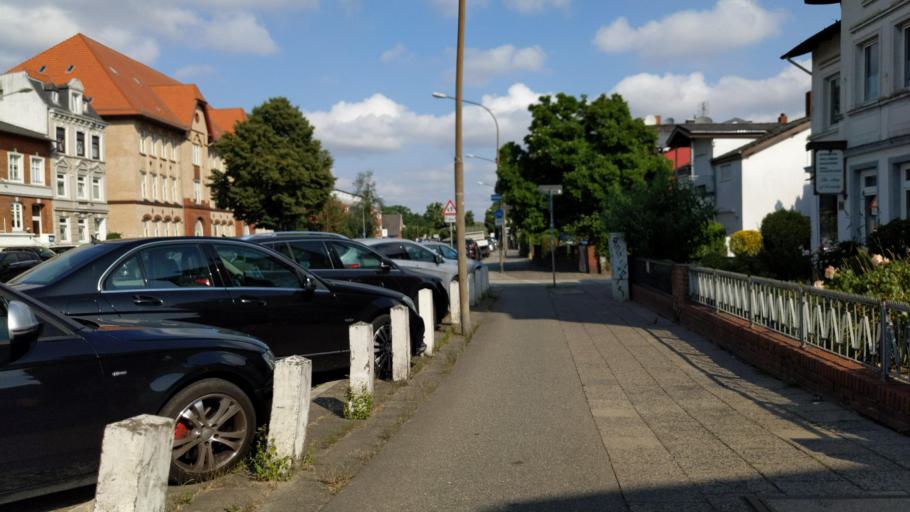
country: DE
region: Schleswig-Holstein
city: Stockelsdorf
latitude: 53.8763
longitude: 10.6630
